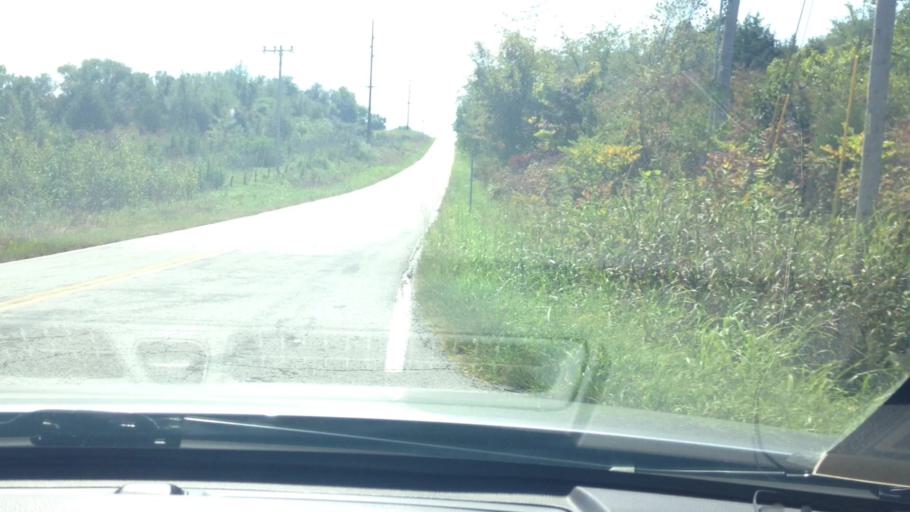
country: US
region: Missouri
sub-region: Platte County
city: Platte City
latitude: 39.3542
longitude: -94.7330
